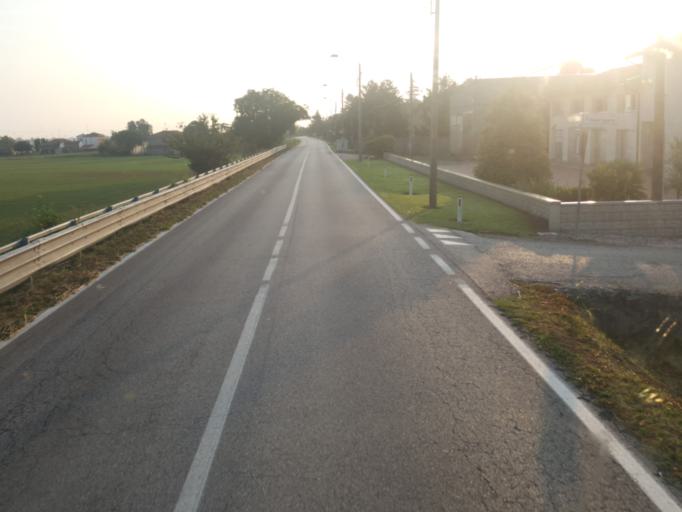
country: IT
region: Emilia-Romagna
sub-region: Provincia di Ferrara
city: San Biagio
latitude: 44.5830
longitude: 11.9007
